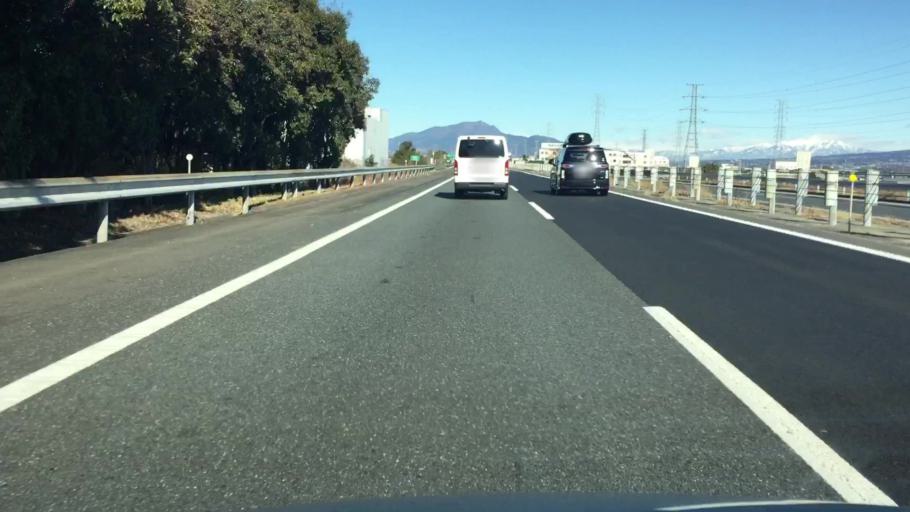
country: JP
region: Gunma
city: Kanekomachi
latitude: 36.3995
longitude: 139.0247
